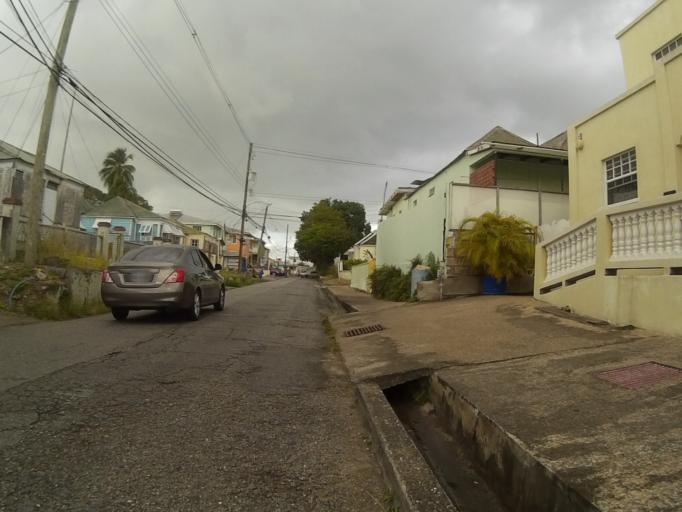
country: BB
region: Saint Michael
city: Bridgetown
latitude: 13.0986
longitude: -59.6034
